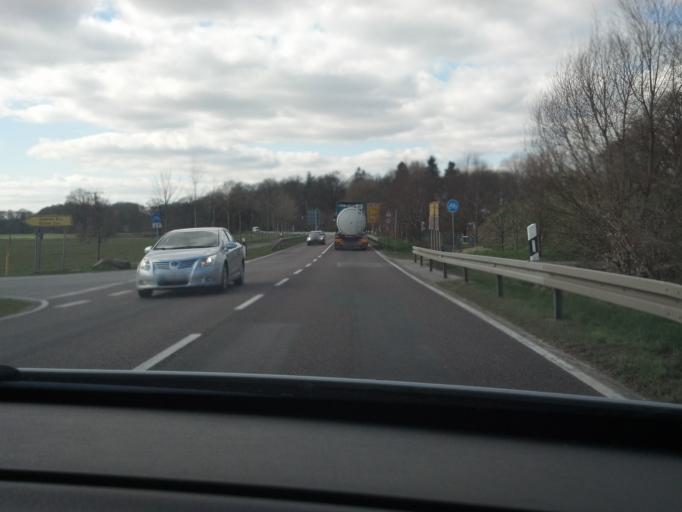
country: DE
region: Mecklenburg-Vorpommern
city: Robel
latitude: 53.3597
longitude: 12.4994
